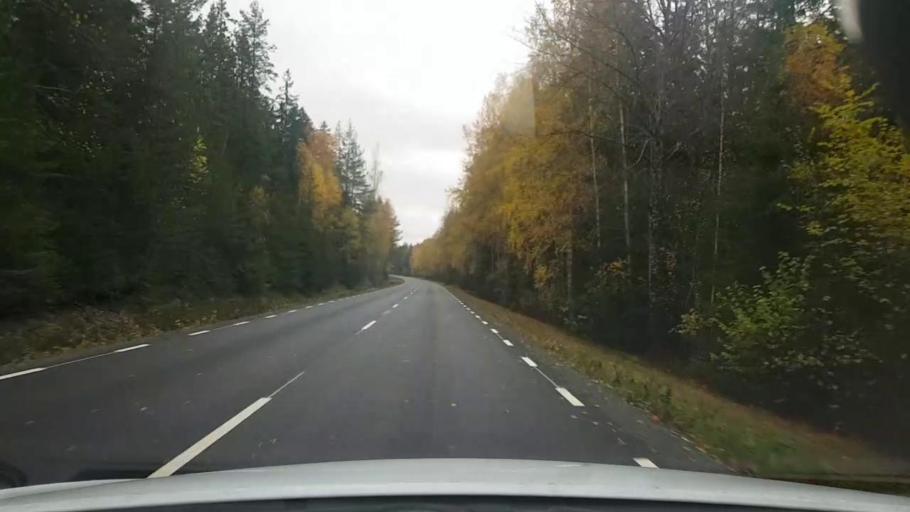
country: SE
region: OErebro
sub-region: Laxa Kommun
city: Laxa
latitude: 58.8060
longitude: 14.5439
